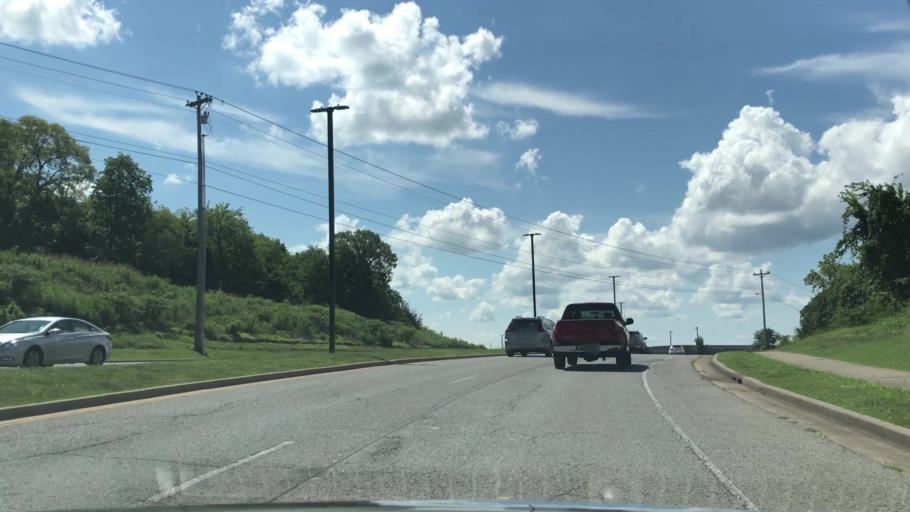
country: US
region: Tennessee
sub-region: Williamson County
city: Franklin
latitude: 35.9252
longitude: -86.8198
